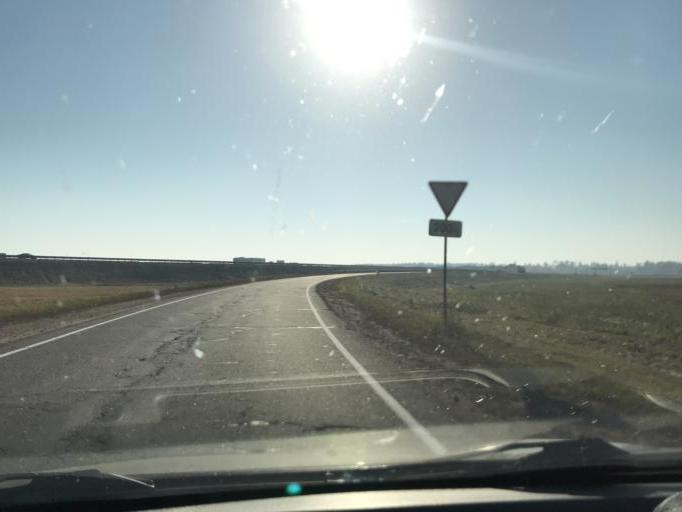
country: BY
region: Minsk
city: Pryvol'ny
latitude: 53.8053
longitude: 27.7899
